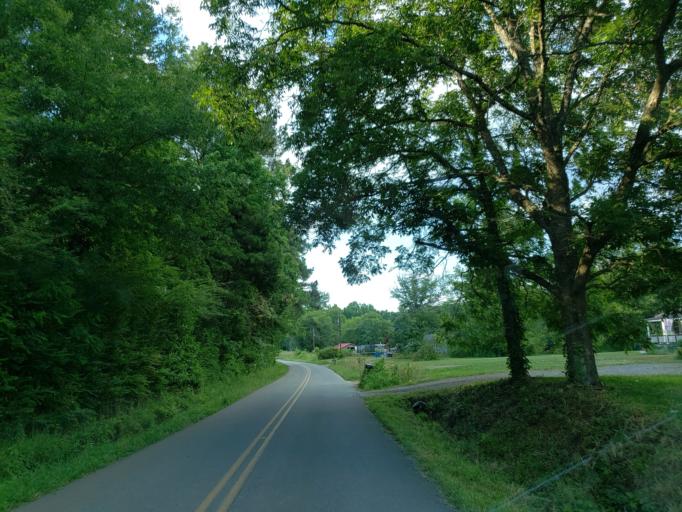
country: US
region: Georgia
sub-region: Haralson County
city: Buchanan
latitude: 33.9137
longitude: -85.2728
